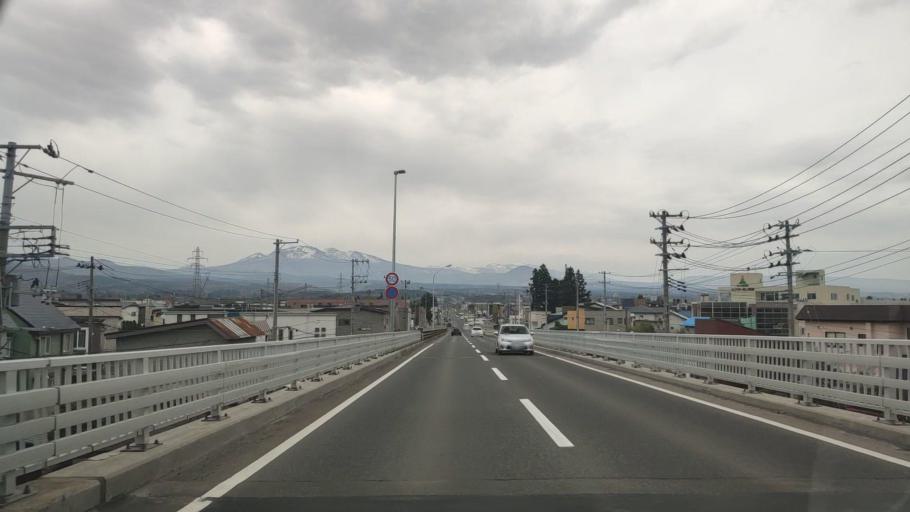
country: JP
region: Aomori
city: Aomori Shi
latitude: 40.8079
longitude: 140.7799
